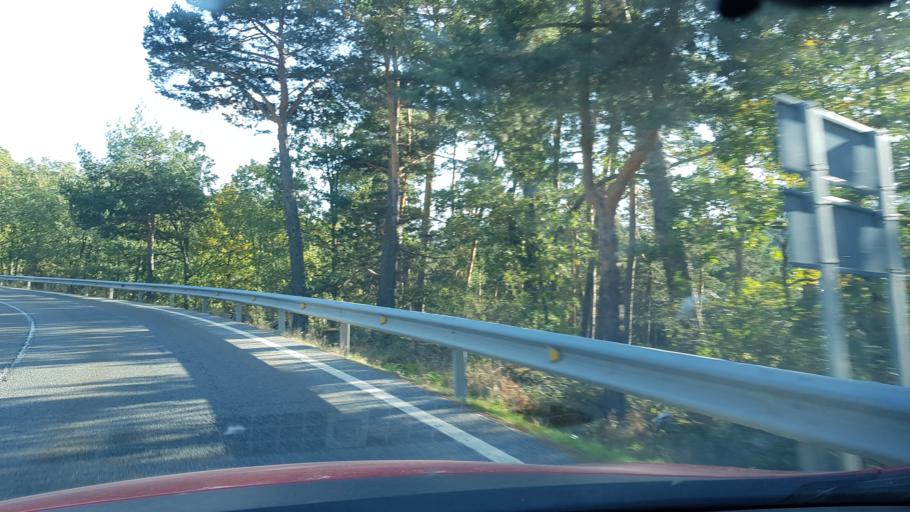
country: ES
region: Castille and Leon
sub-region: Provincia de Segovia
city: San Ildefonso
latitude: 40.8523
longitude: -4.0281
